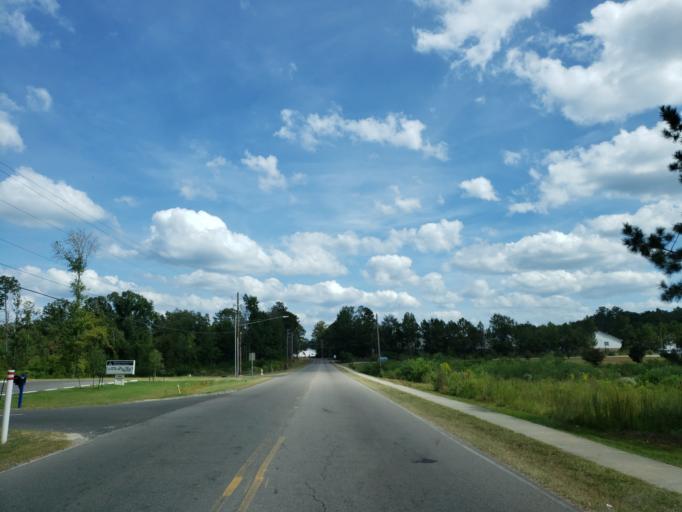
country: US
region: Mississippi
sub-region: Forrest County
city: Hattiesburg
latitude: 31.2992
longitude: -89.3000
